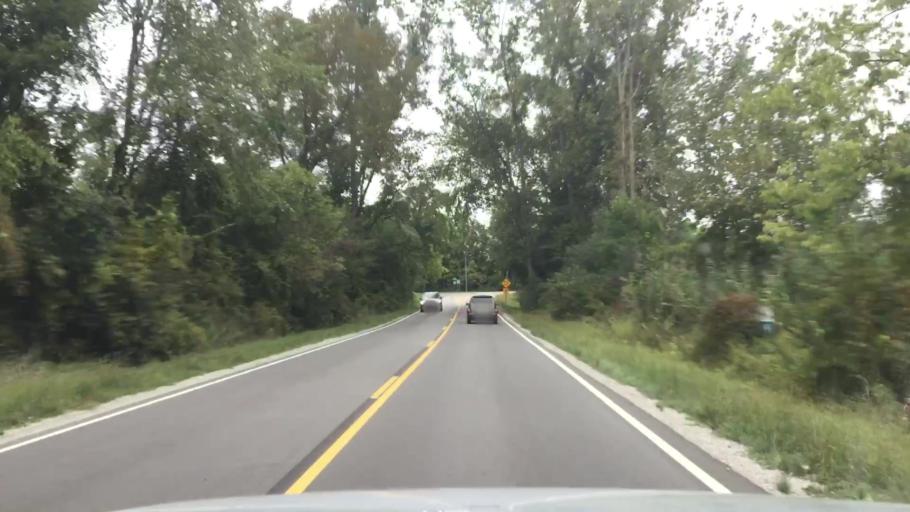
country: US
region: Michigan
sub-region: Washtenaw County
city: Ypsilanti
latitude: 42.2075
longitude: -83.6210
